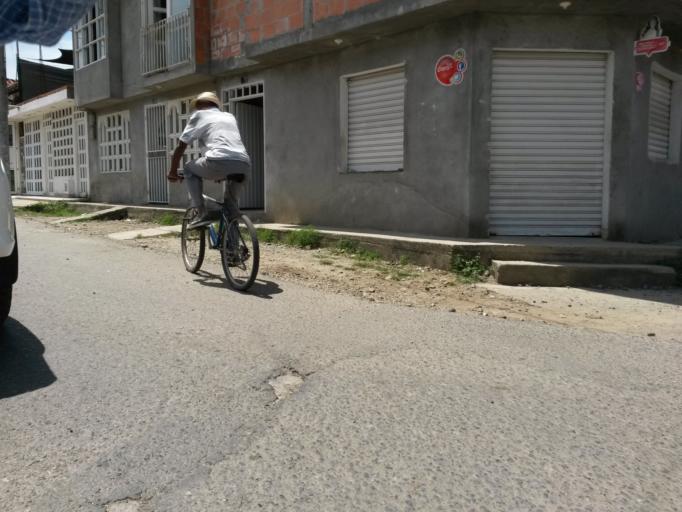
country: CO
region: Cauca
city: Santander de Quilichao
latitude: 3.0153
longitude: -76.4802
